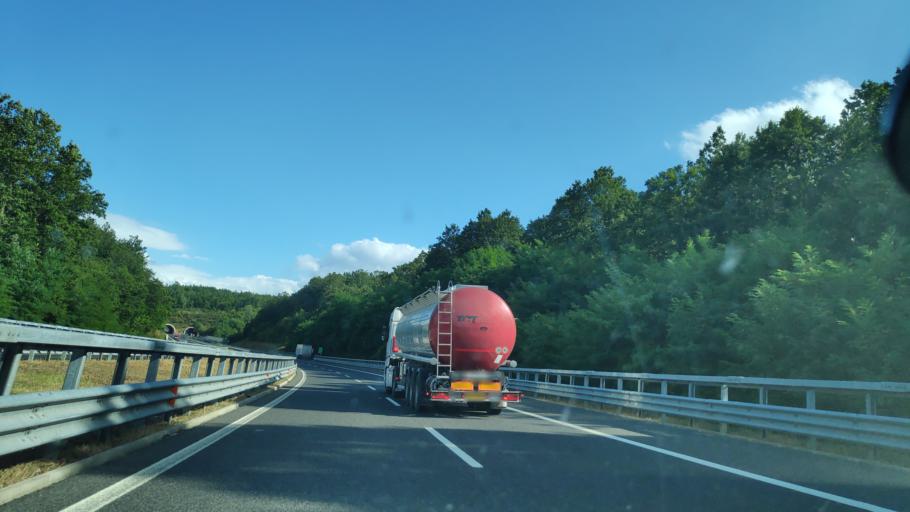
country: IT
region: Campania
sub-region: Provincia di Salerno
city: Casalbuono
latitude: 40.2387
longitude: 15.6602
